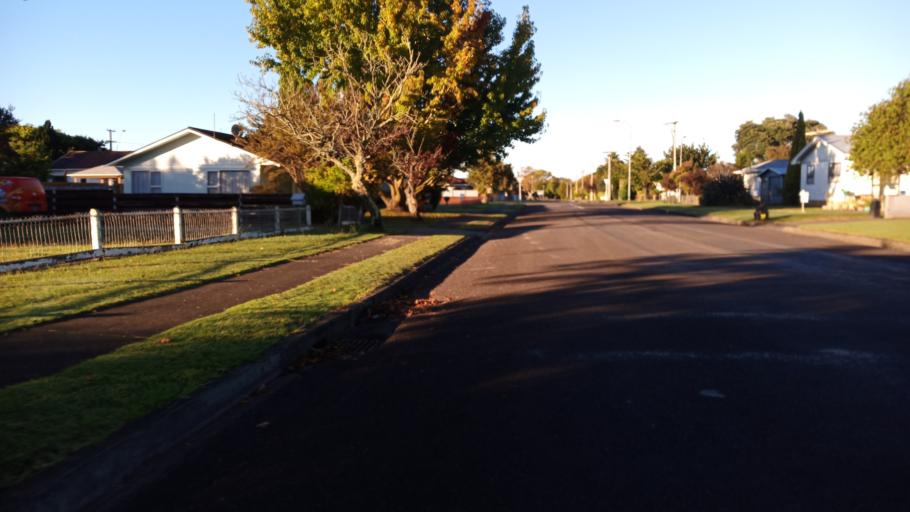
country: NZ
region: Gisborne
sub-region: Gisborne District
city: Gisborne
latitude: -38.6549
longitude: 177.9909
